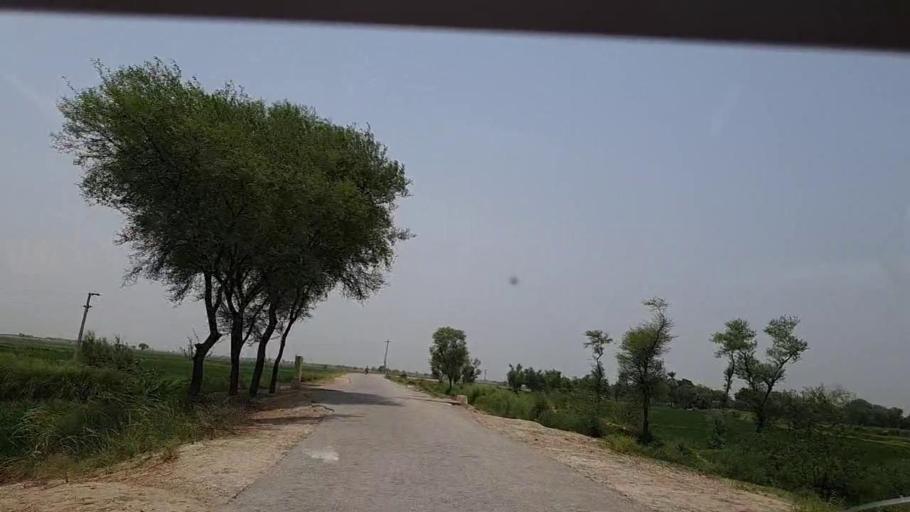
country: PK
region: Sindh
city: Khairpur Nathan Shah
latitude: 27.0078
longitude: 67.6707
